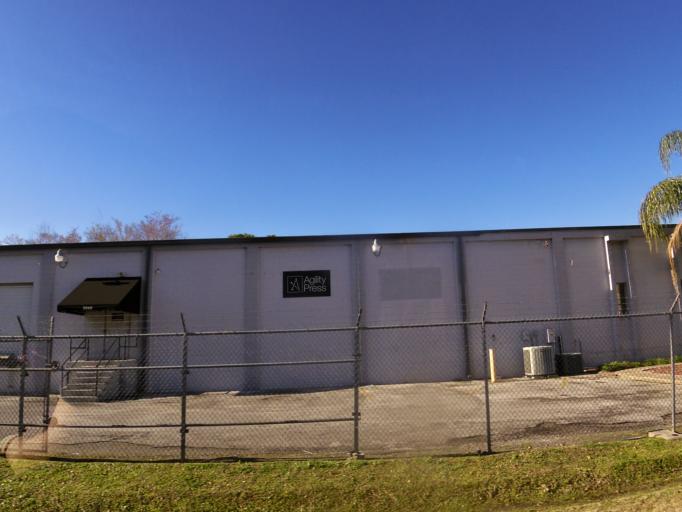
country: US
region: Florida
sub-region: Duval County
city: Jacksonville
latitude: 30.2697
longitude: -81.6251
